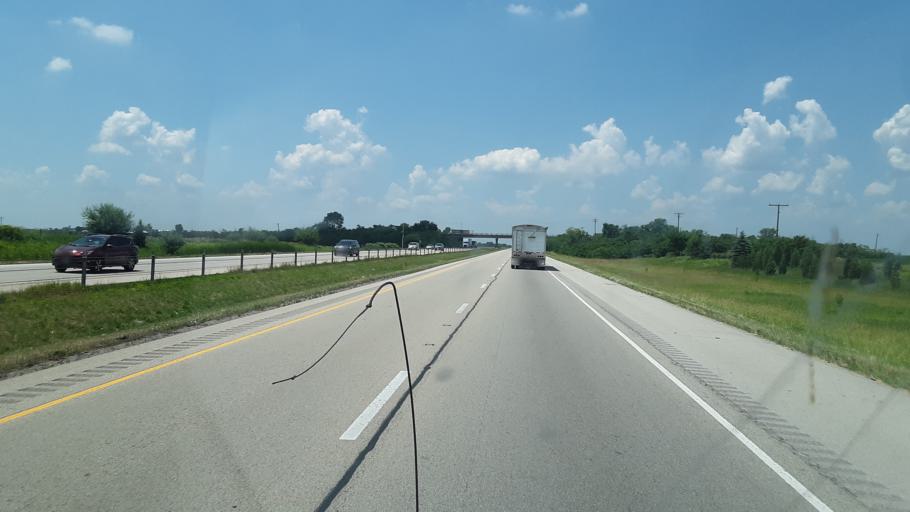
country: US
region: Illinois
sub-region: LaSalle County
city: Seneca
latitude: 41.3762
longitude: -88.6271
